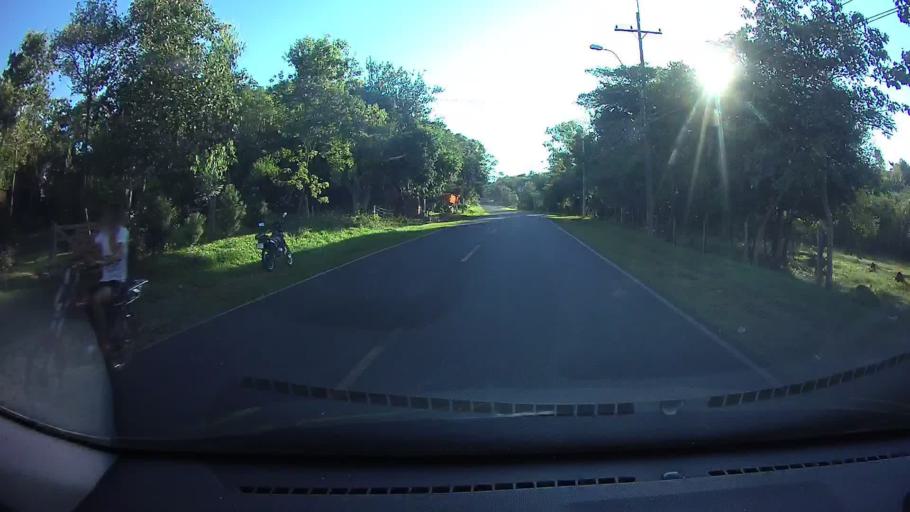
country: PY
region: Cordillera
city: Emboscada
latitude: -25.1936
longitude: -57.3146
